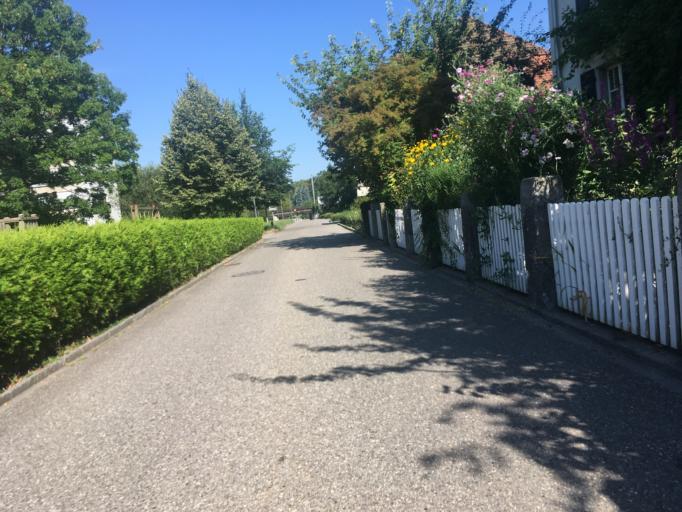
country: CH
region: Bern
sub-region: Emmental District
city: Burgdorf
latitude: 47.0598
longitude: 7.6295
